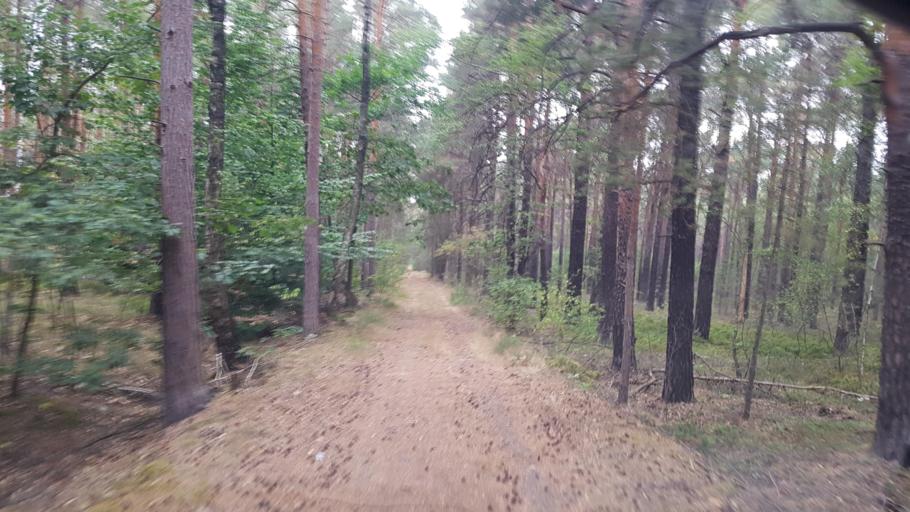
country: DE
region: Brandenburg
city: Sallgast
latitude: 51.6028
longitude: 13.8301
